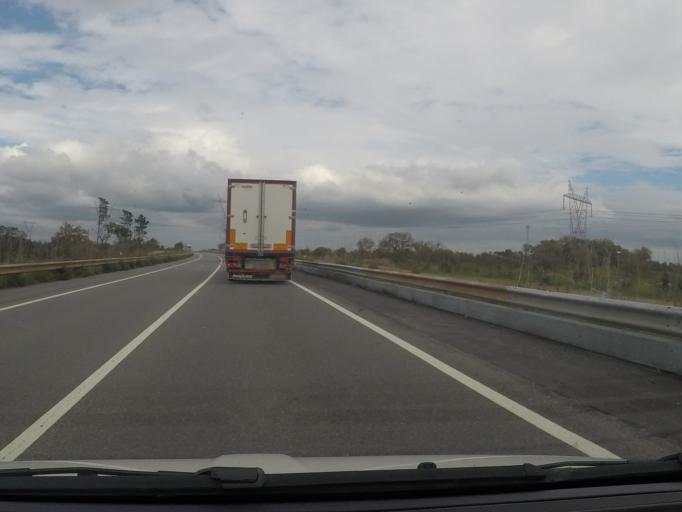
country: PT
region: Setubal
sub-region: Santiago do Cacem
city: Santiago do Cacem
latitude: 38.0711
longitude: -8.6581
